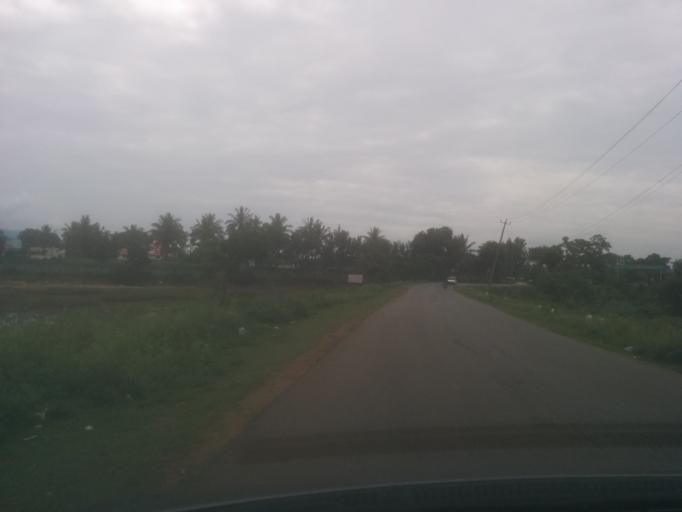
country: IN
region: Karnataka
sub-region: Chikmagalur
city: Chikmagalur
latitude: 13.3529
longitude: 75.7614
